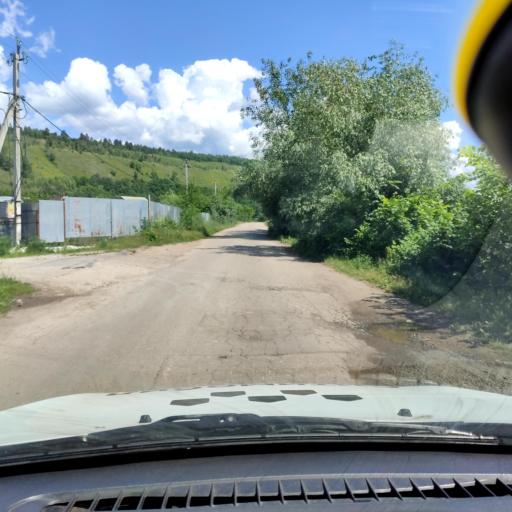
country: RU
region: Samara
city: Povolzhskiy
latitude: 53.4685
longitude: 49.6706
